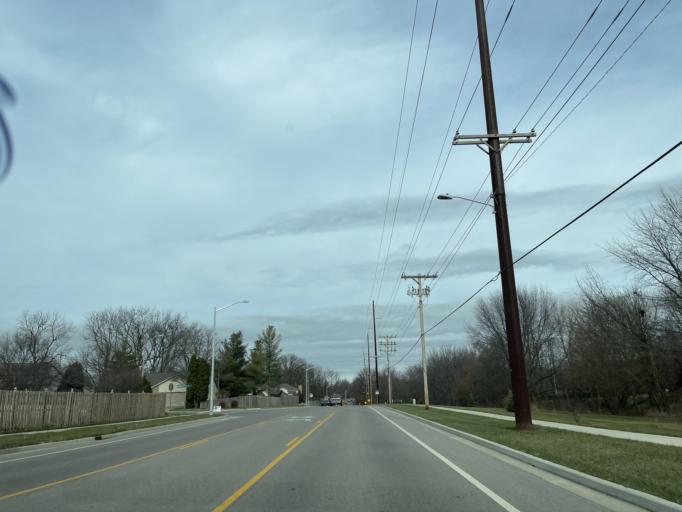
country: US
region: Illinois
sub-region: Sangamon County
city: Jerome
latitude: 39.7756
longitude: -89.7346
